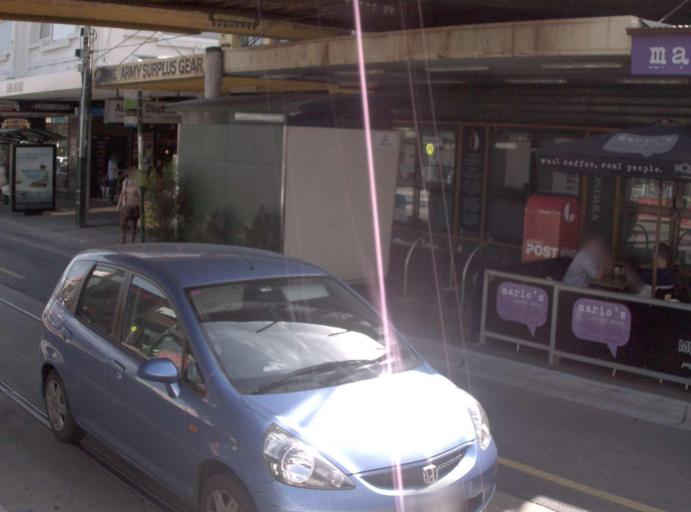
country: AU
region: Victoria
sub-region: Boroondara
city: Hawthorn East
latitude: -37.8215
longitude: 145.0355
